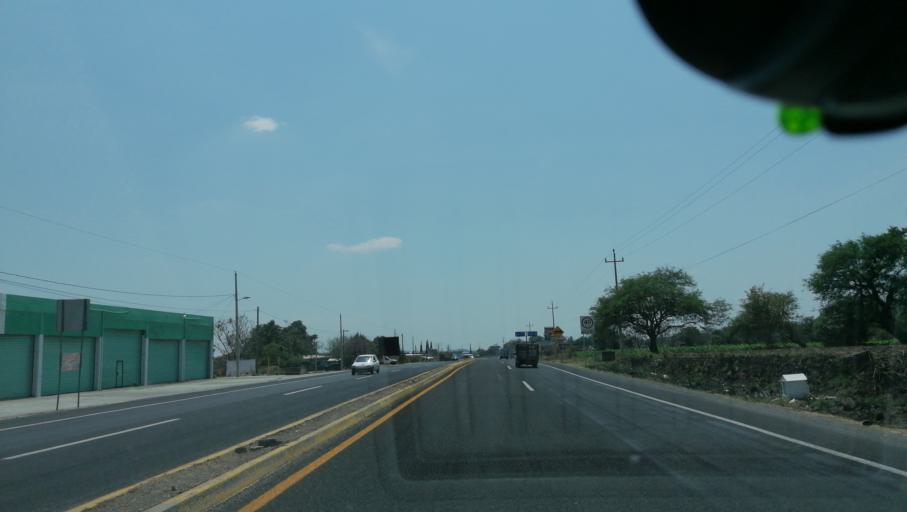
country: MX
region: Puebla
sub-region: Huaquechula
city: Tronconal
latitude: 18.7954
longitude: -98.4522
